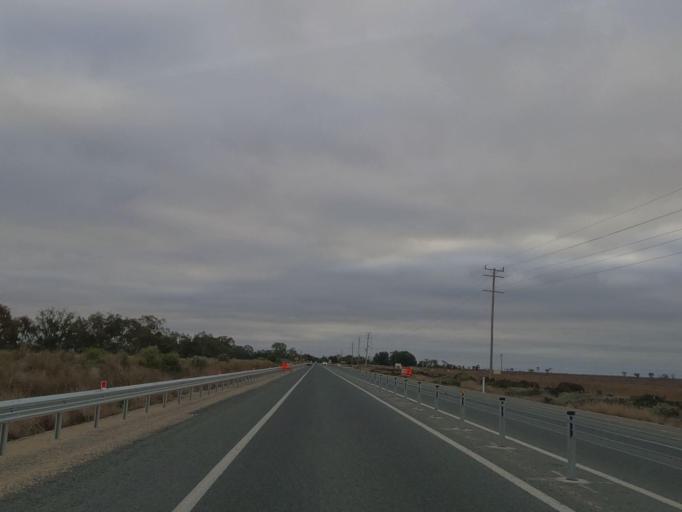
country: AU
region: Victoria
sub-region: Swan Hill
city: Swan Hill
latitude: -35.5405
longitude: 143.7525
